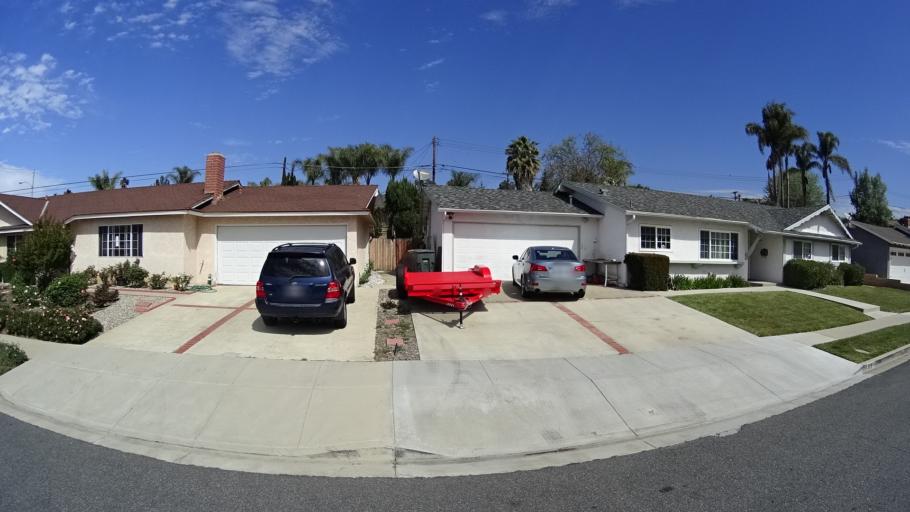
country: US
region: California
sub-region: Ventura County
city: Casa Conejo
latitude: 34.1873
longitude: -118.9393
